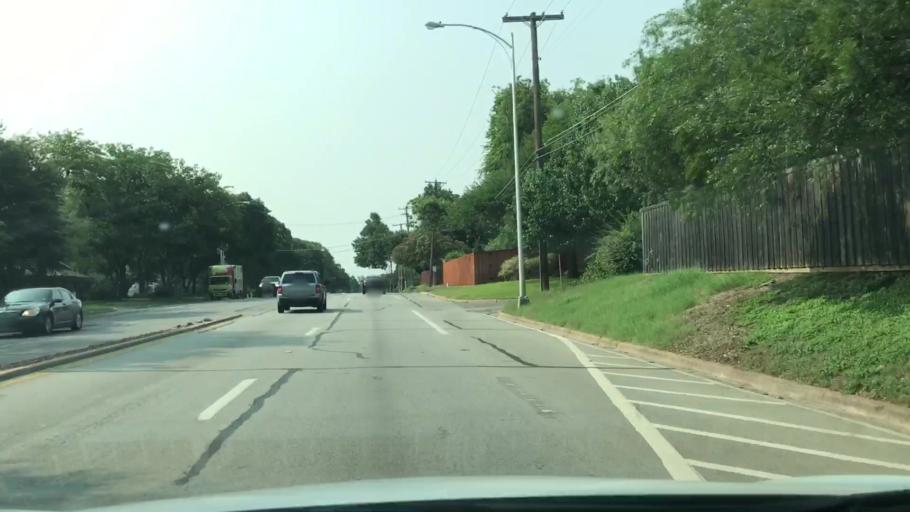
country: US
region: Texas
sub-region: Dallas County
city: Dallas
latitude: 32.7633
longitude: -96.8358
